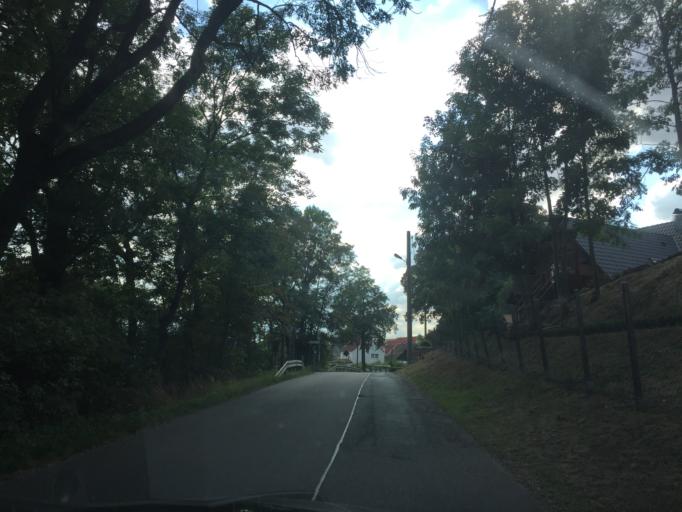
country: DE
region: Thuringia
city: Nobitz
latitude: 50.9674
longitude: 12.4614
